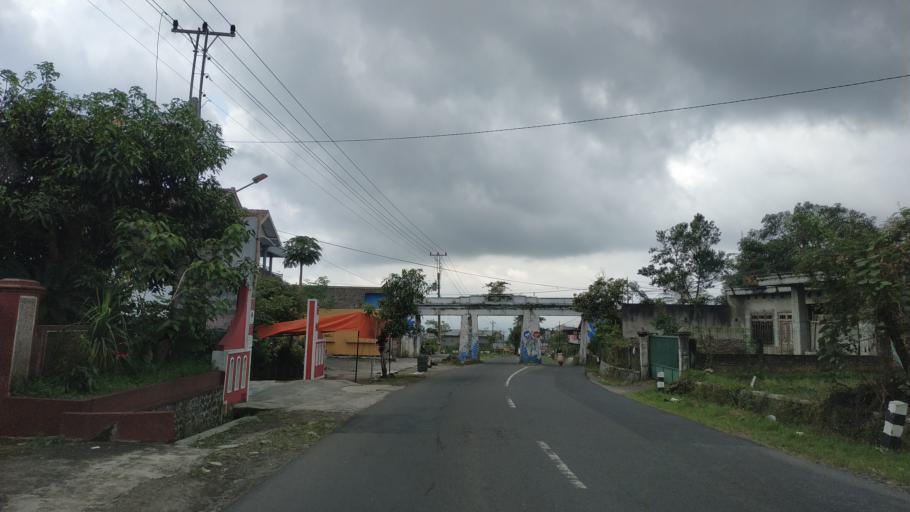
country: ID
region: Central Java
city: Magelang
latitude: -7.2858
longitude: 110.1187
